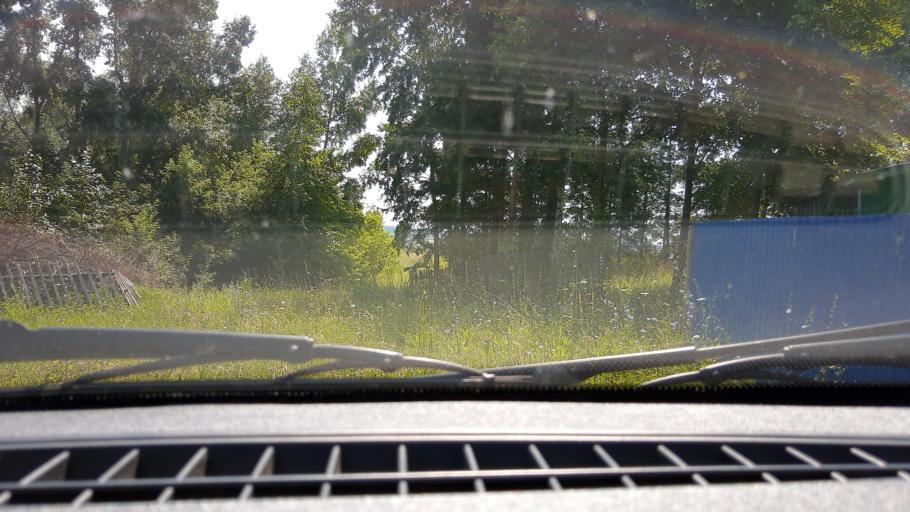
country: RU
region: Bashkortostan
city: Kushnarenkovo
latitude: 55.0728
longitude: 55.1646
